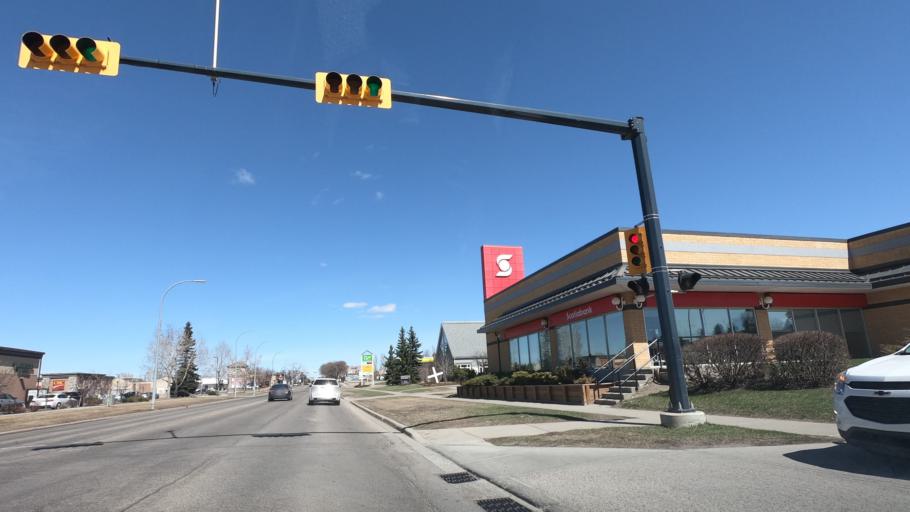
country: CA
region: Alberta
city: Airdrie
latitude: 51.2892
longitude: -114.0134
